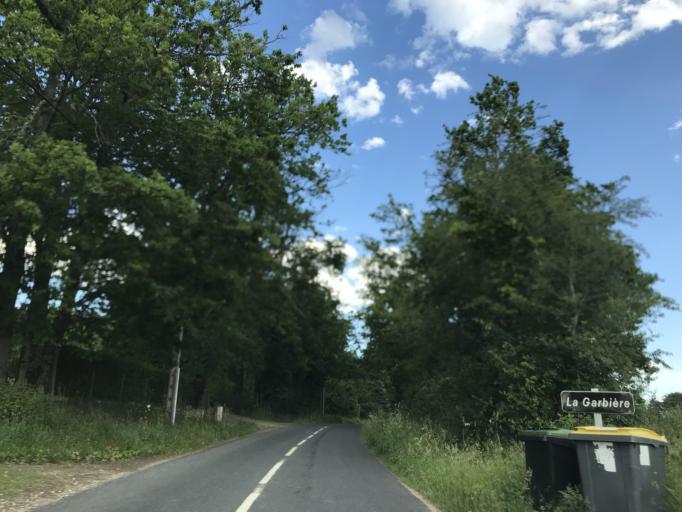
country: FR
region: Auvergne
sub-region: Departement du Puy-de-Dome
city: Courpiere
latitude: 45.7718
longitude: 3.5975
